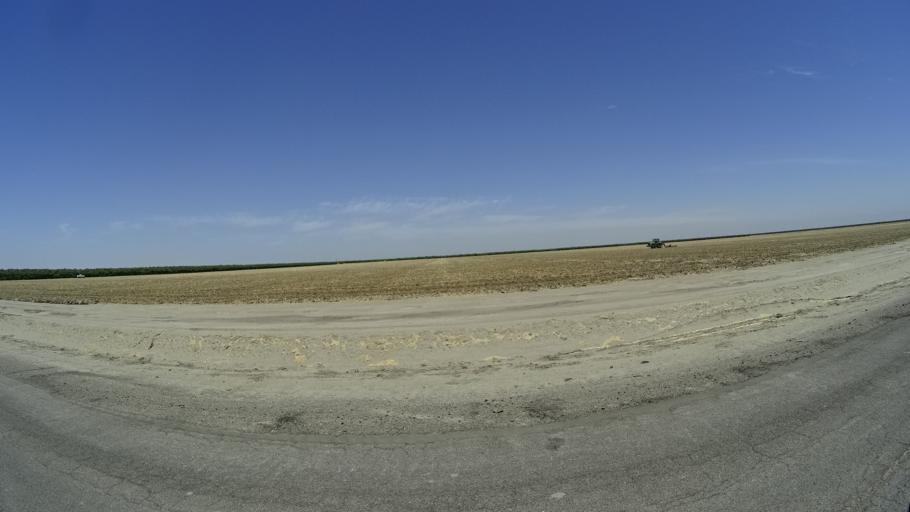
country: US
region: California
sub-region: Kings County
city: Corcoran
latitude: 36.1089
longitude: -119.6158
